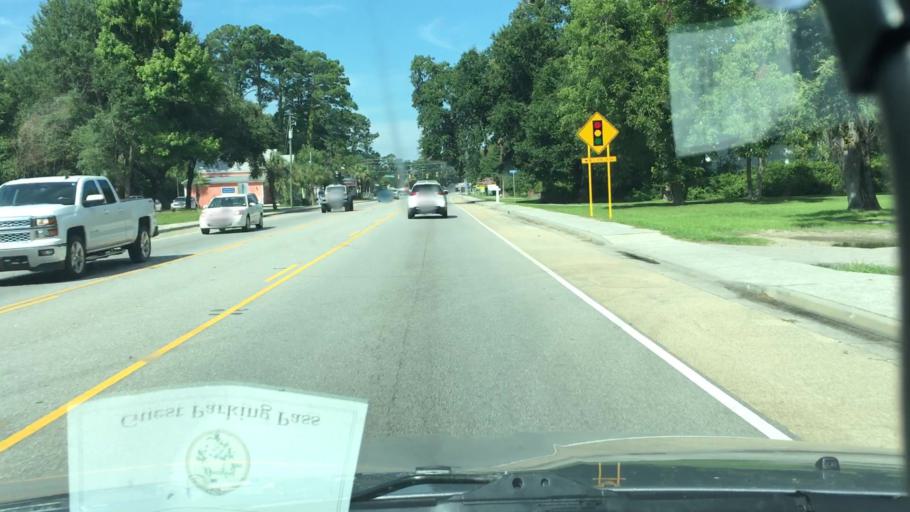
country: US
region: South Carolina
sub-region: Beaufort County
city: Beaufort
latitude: 32.3978
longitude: -80.5740
